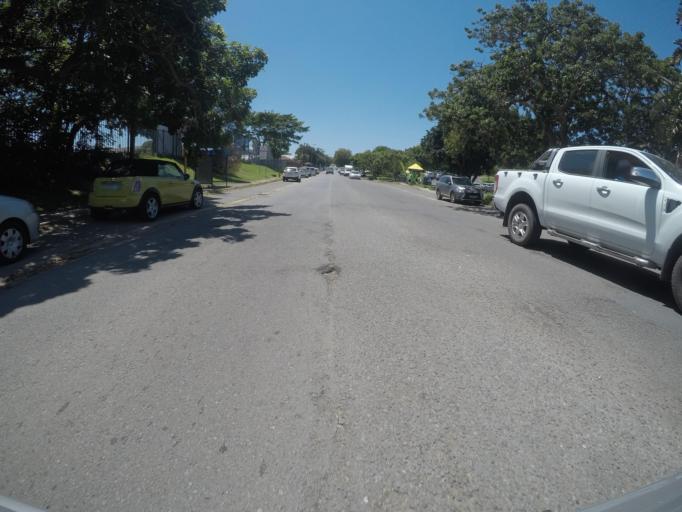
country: ZA
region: Eastern Cape
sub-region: Buffalo City Metropolitan Municipality
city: East London
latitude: -32.9902
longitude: 27.9020
